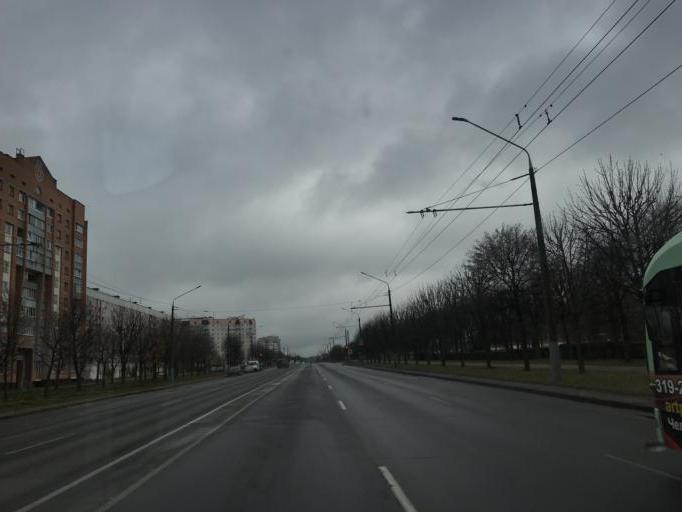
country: BY
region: Mogilev
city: Mahilyow
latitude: 53.8698
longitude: 30.3248
